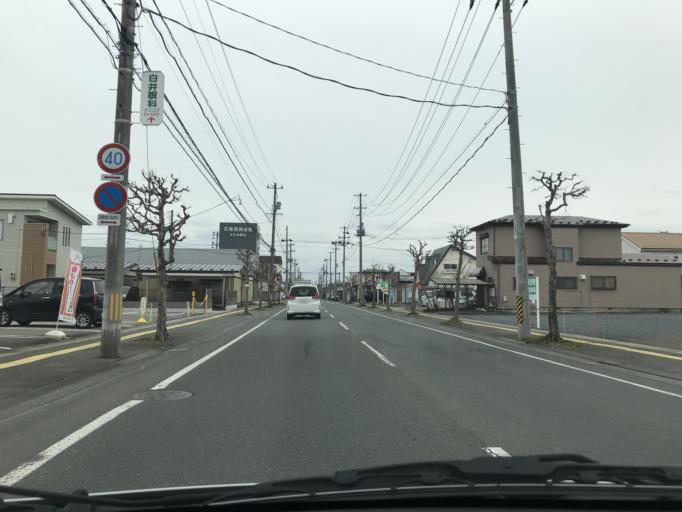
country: JP
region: Iwate
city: Hanamaki
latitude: 39.3925
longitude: 141.1079
